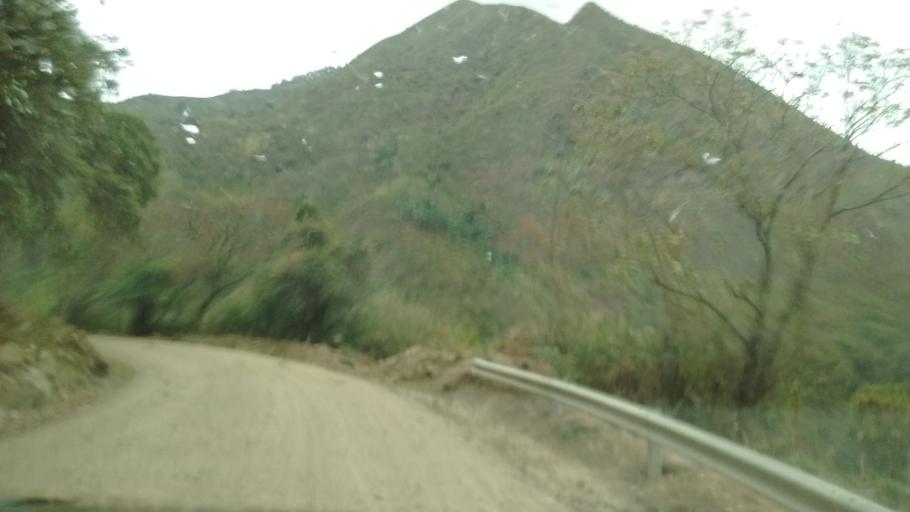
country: CO
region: Cauca
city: La Vega
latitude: 2.0346
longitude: -76.7965
